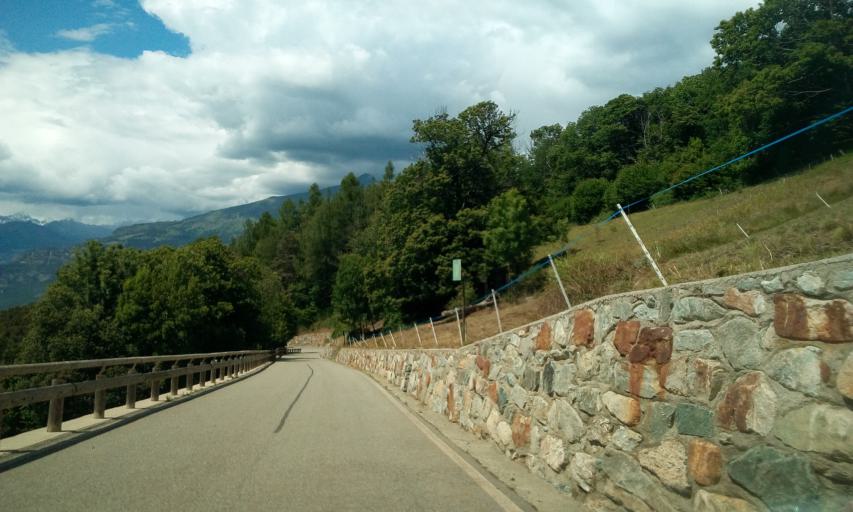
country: IT
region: Aosta Valley
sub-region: Valle d'Aosta
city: Challand-Saint-Victor
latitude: 45.7018
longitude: 7.6985
